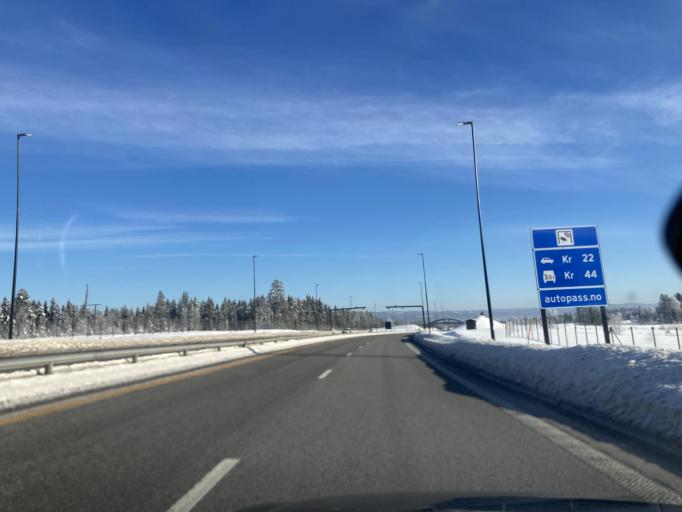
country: NO
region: Hedmark
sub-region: Elverum
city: Elverum
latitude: 60.8771
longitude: 11.4522
